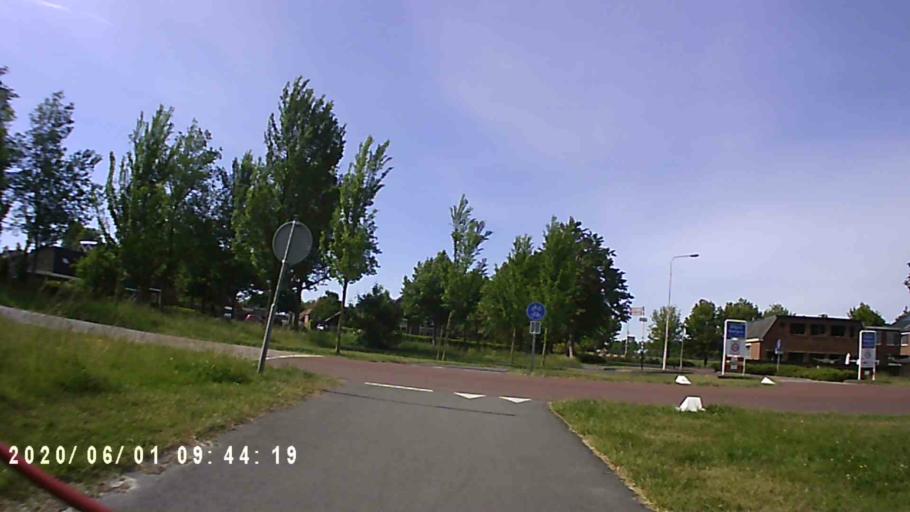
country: NL
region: Friesland
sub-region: Menameradiel
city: Menaam
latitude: 53.2385
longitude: 5.6843
